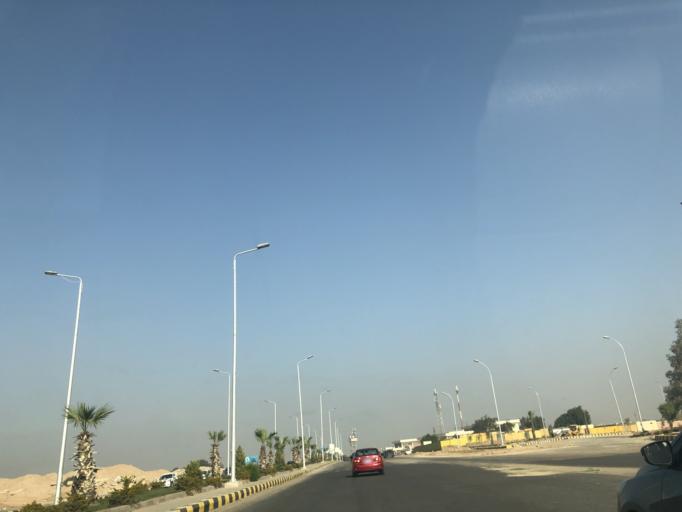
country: EG
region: Al Jizah
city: Madinat Sittah Uktubar
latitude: 29.9523
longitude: 31.0735
